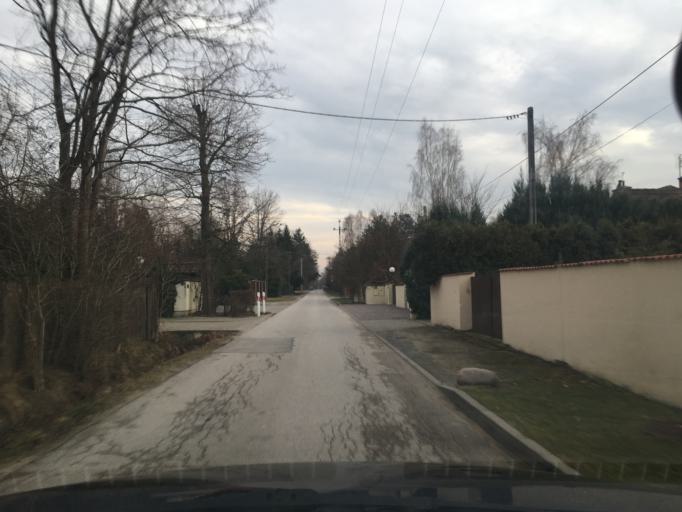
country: PL
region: Masovian Voivodeship
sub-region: Powiat piaseczynski
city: Lesznowola
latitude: 52.0392
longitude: 20.9538
